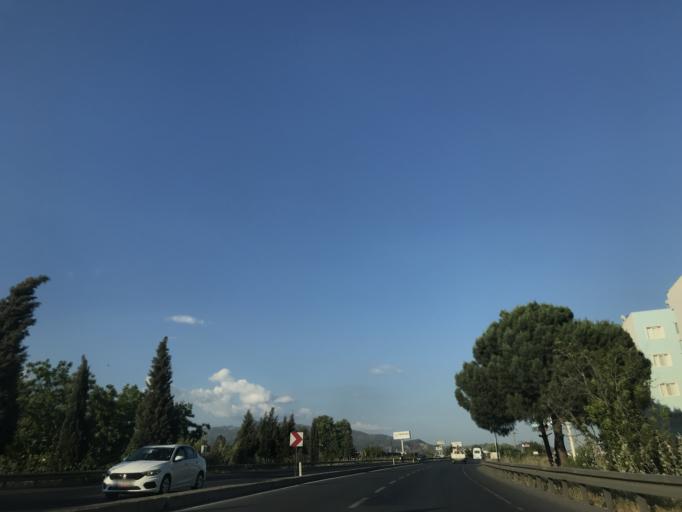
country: TR
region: Aydin
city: Umurlu
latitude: 37.8543
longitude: 27.9759
